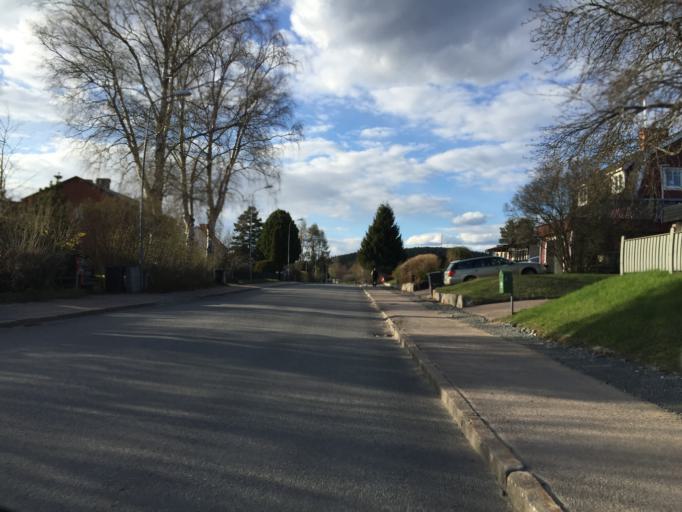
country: SE
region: Dalarna
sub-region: Ludvika Kommun
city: Ludvika
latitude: 60.1215
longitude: 15.1928
